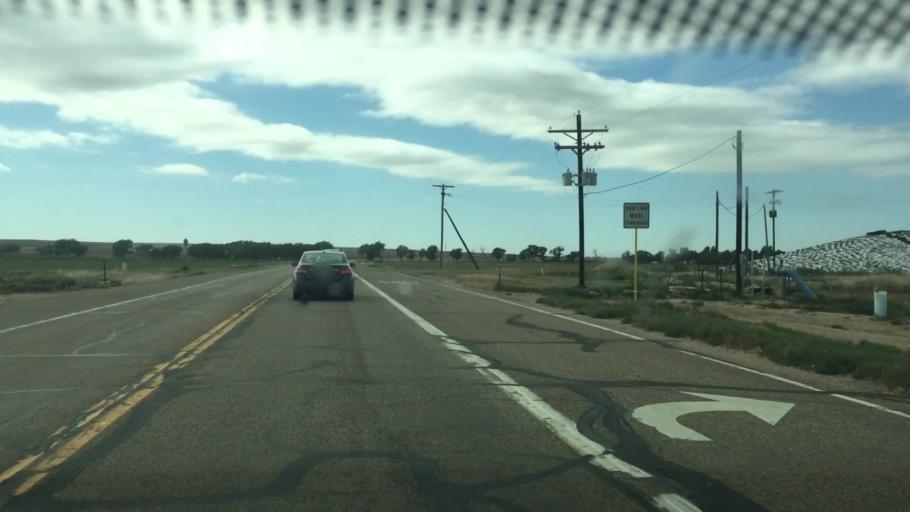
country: US
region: Colorado
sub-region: Prowers County
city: Lamar
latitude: 38.0640
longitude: -102.3452
